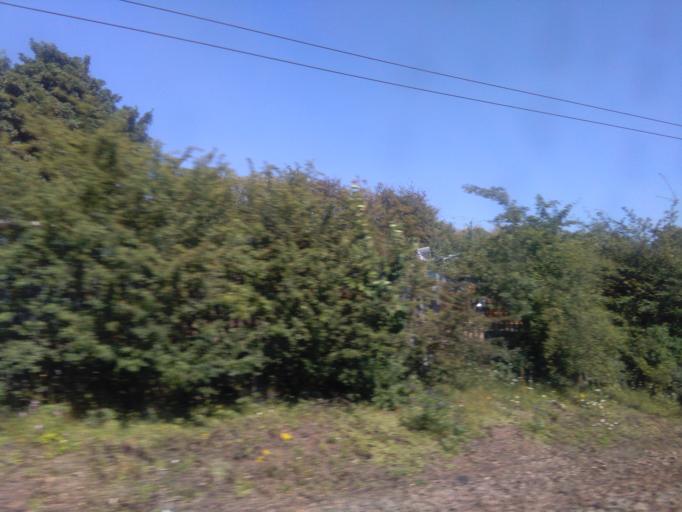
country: GB
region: England
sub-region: Hertfordshire
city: Harpenden
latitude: 51.8502
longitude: -0.3694
